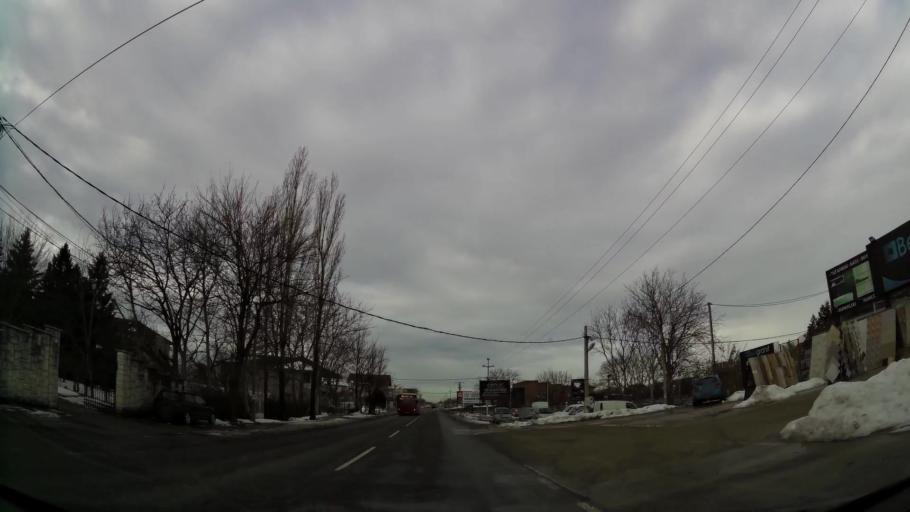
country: RS
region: Central Serbia
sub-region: Belgrade
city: Surcin
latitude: 44.7976
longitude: 20.3140
